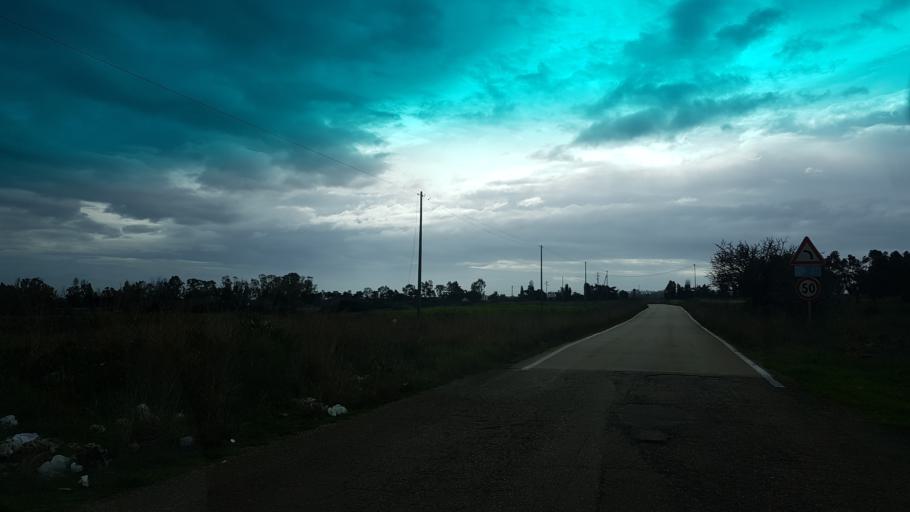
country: IT
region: Apulia
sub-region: Provincia di Brindisi
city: San Vito dei Normanni
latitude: 40.7157
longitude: 17.7654
